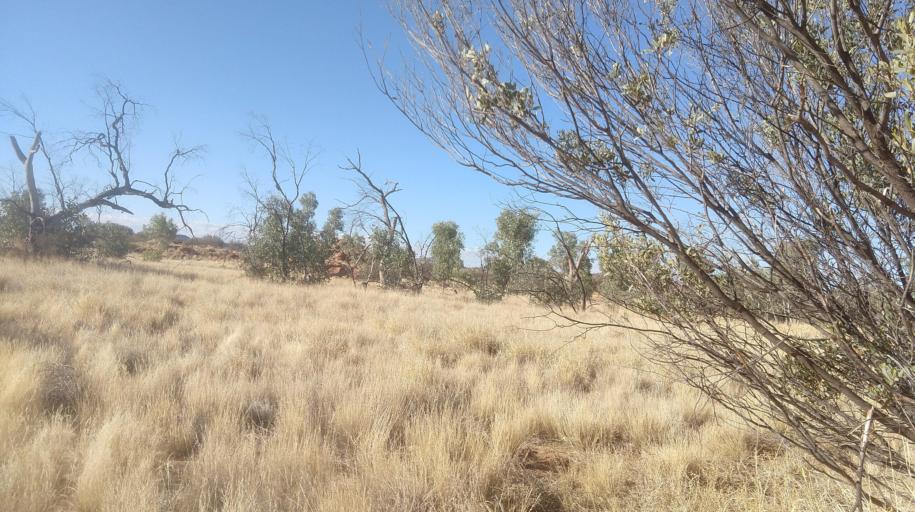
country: AU
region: Northern Territory
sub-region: Alice Springs
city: Alice Springs
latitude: -23.6694
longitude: 133.8838
